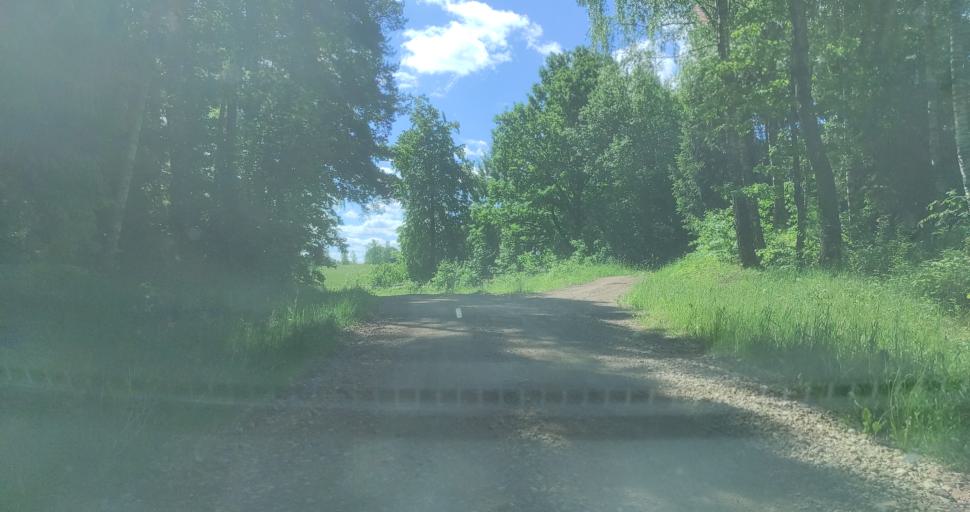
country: LV
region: Alsunga
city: Alsunga
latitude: 56.8898
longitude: 21.7154
